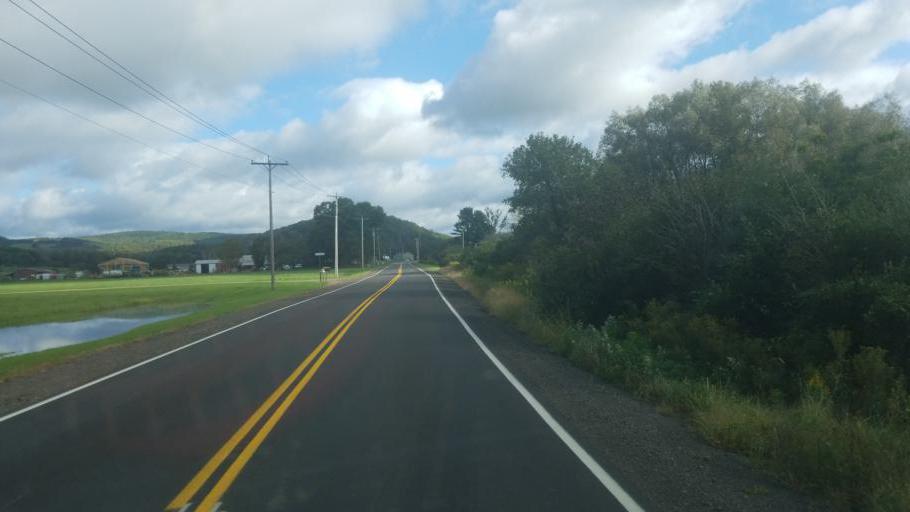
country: US
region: New York
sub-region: Cattaraugus County
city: Weston Mills
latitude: 42.0840
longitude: -78.3678
